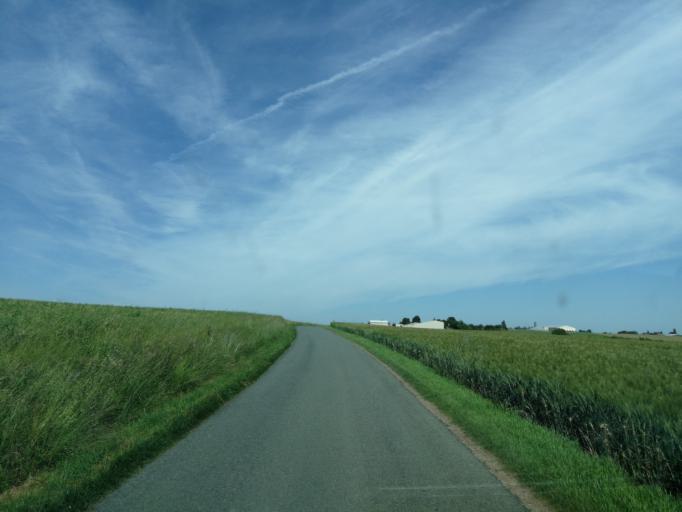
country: FR
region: Pays de la Loire
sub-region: Departement de la Vendee
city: Le Langon
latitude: 46.4375
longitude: -0.8879
